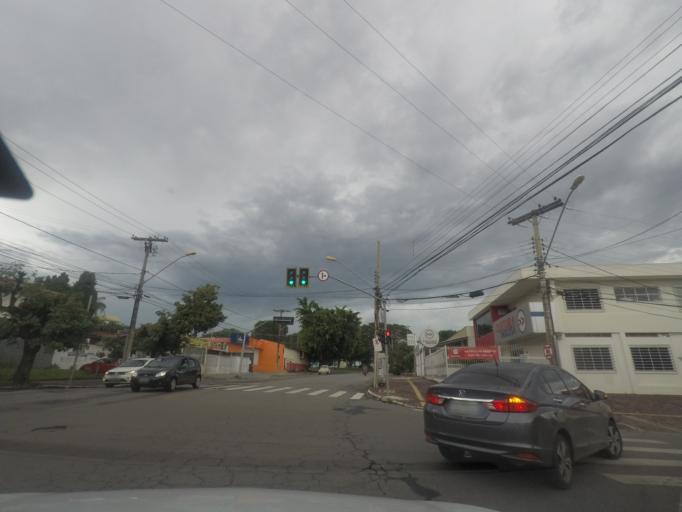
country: BR
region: Goias
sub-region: Goiania
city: Goiania
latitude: -16.6892
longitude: -49.2521
